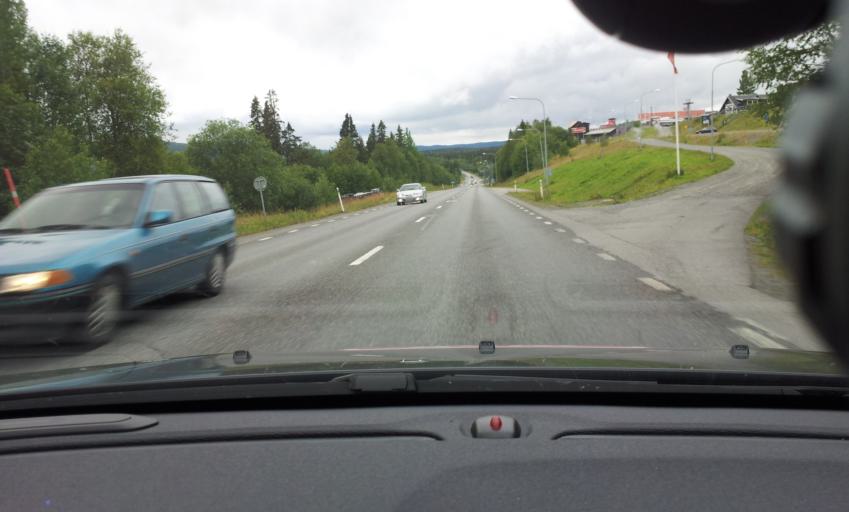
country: SE
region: Jaemtland
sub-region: Are Kommun
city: Are
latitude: 63.3953
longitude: 12.9315
